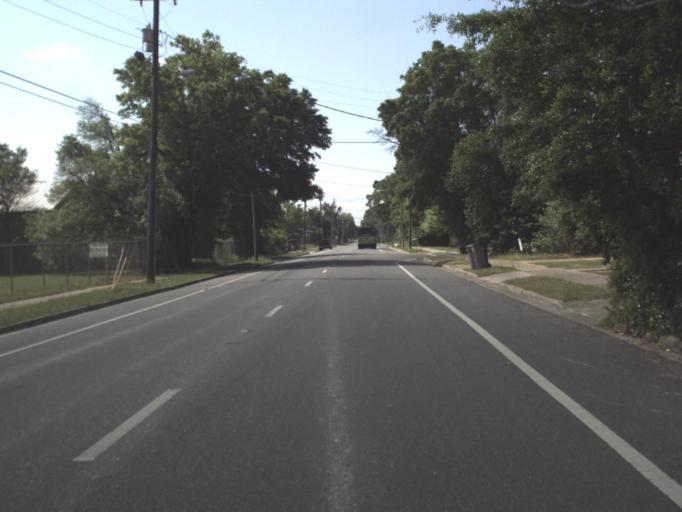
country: US
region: Florida
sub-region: Escambia County
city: Goulding
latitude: 30.4467
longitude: -87.2168
